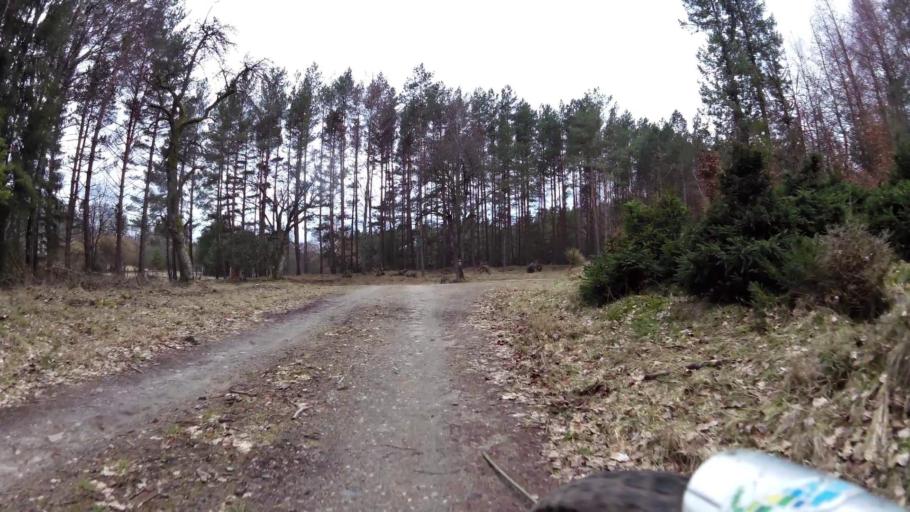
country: PL
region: Pomeranian Voivodeship
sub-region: Powiat bytowski
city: Trzebielino
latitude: 54.1427
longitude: 17.1498
